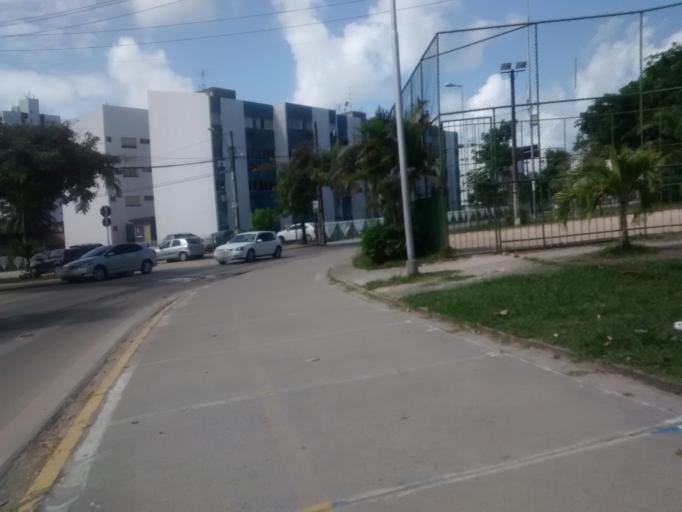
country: BR
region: Pernambuco
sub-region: Recife
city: Recife
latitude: -8.0928
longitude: -34.9162
